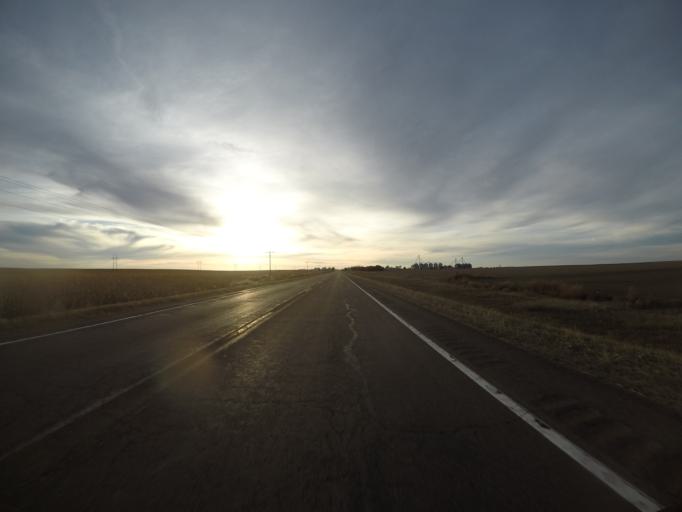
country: US
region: Colorado
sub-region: Washington County
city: Akron
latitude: 39.7414
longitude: -103.2073
